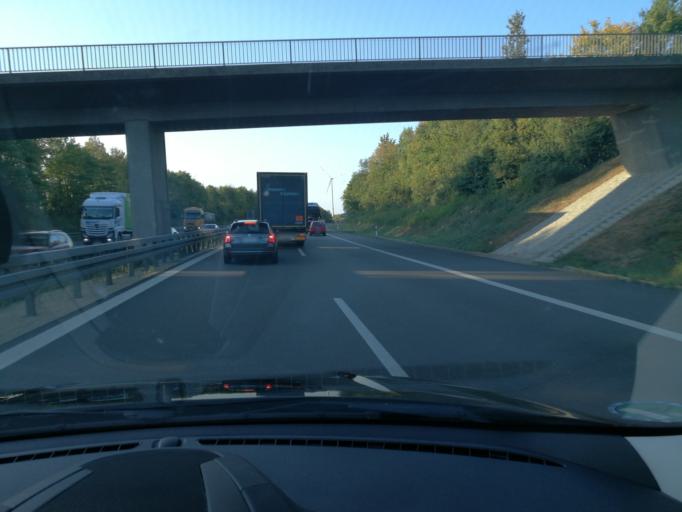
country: DE
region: Bavaria
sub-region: Upper Palatinate
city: Pilsach
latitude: 49.2995
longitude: 11.5512
